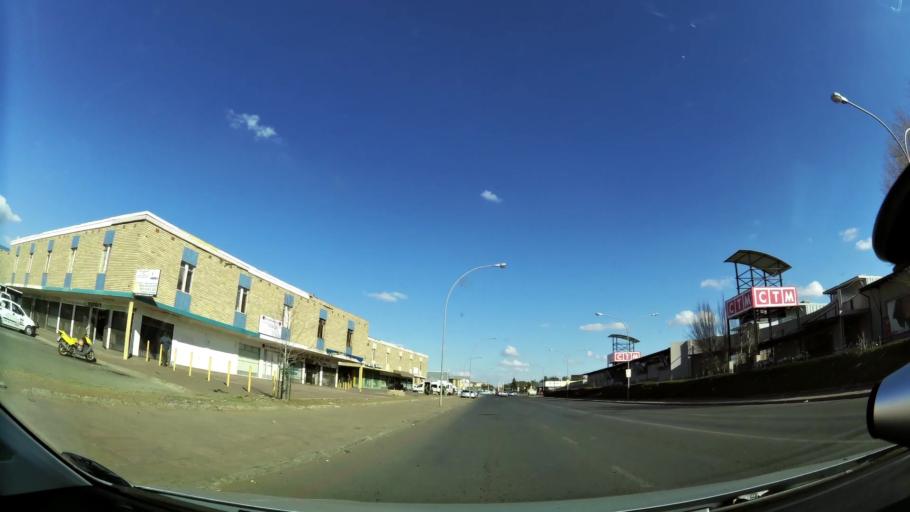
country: ZA
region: Northern Cape
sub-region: Frances Baard District Municipality
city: Kimberley
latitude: -28.7341
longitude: 24.7603
